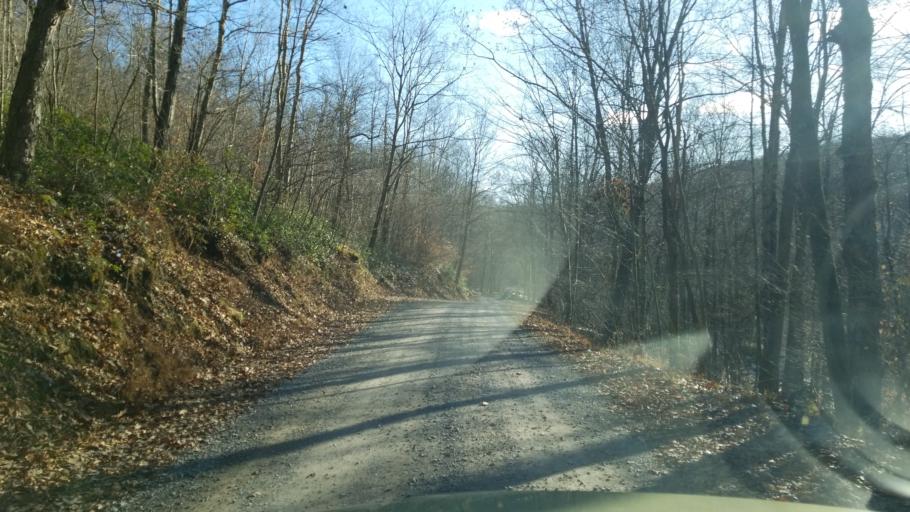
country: US
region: Pennsylvania
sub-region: Jefferson County
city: Brockway
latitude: 41.2842
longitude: -78.8263
